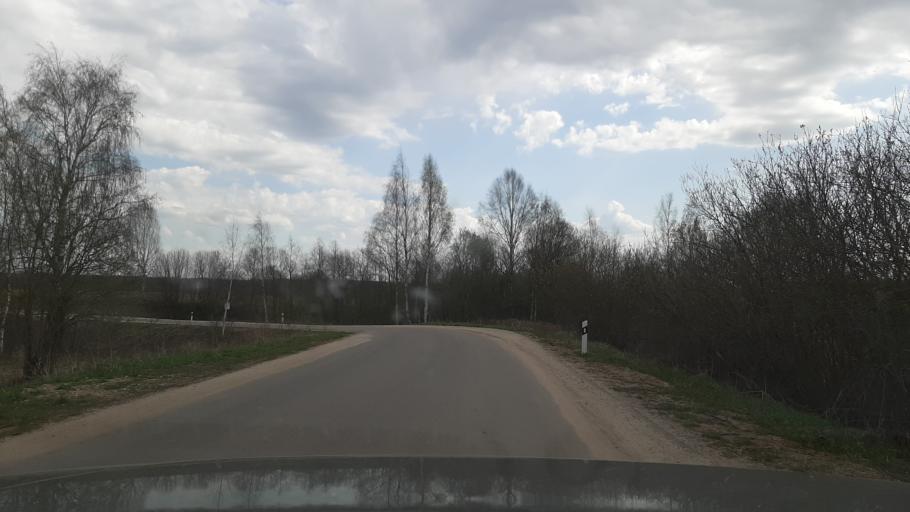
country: RU
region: Ivanovo
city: Furmanov
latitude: 57.3202
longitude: 41.1617
